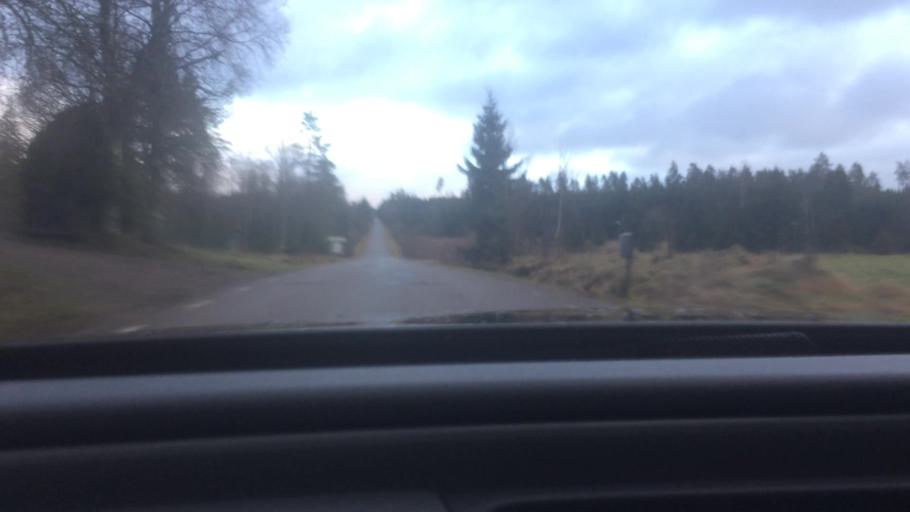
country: SE
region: Vaestra Goetaland
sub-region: Falkopings Kommun
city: Falkoeping
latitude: 57.9982
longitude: 13.4812
